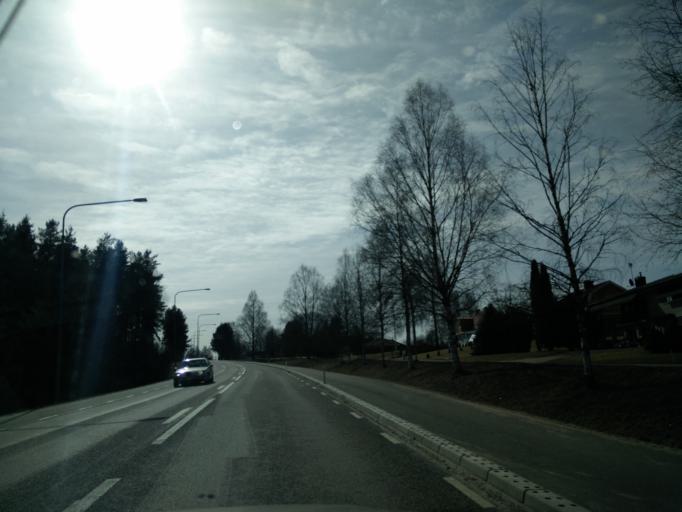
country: SE
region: Vaermland
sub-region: Hagfors Kommun
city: Hagfors
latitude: 60.0174
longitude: 13.6835
